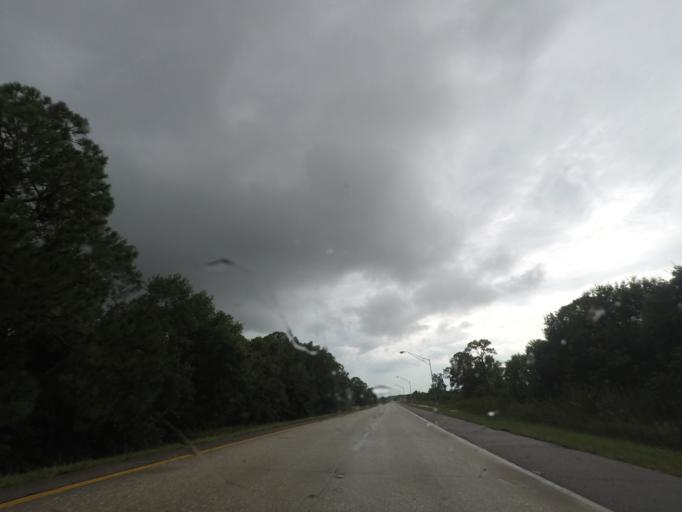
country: US
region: Florida
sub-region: Pinellas County
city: Pinellas Park
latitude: 27.8551
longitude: -82.6650
